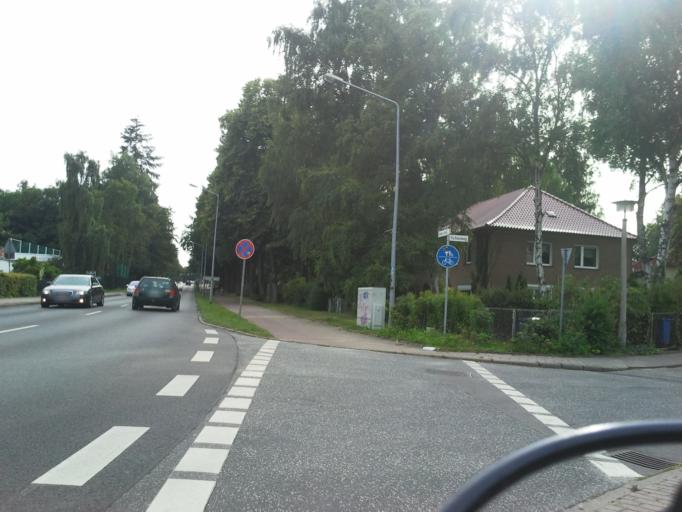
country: DE
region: Mecklenburg-Vorpommern
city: Kritzmow
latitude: 54.0755
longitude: 12.0927
